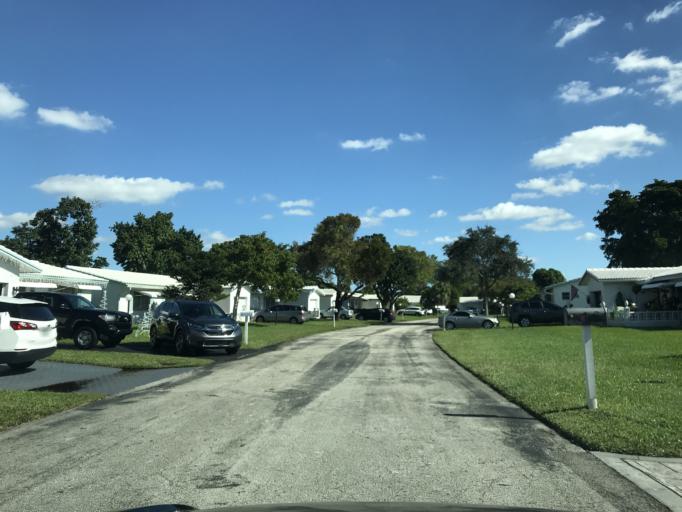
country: US
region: Florida
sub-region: Broward County
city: Plantation
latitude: 26.1405
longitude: -80.2614
